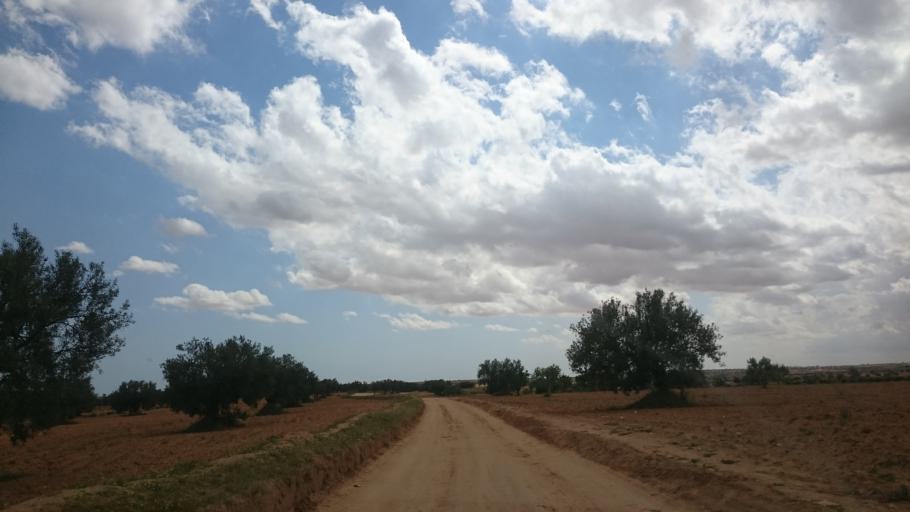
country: TN
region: Safaqis
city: Sfax
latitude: 34.7516
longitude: 10.4880
